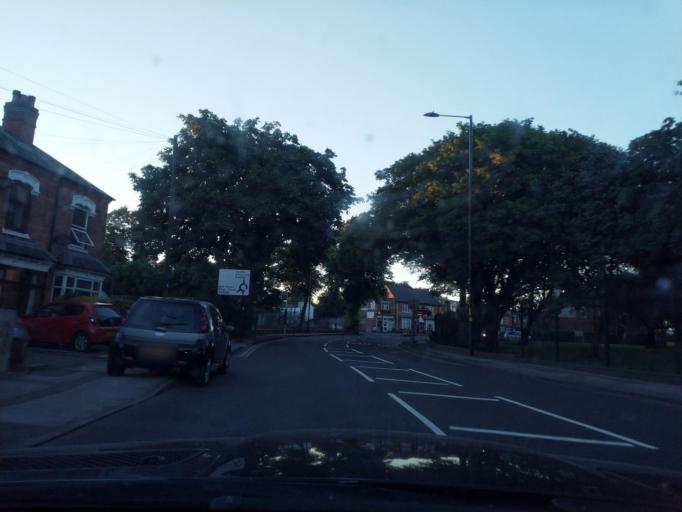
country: GB
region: England
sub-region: City and Borough of Birmingham
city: Acocks Green
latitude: 52.4584
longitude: -1.8181
